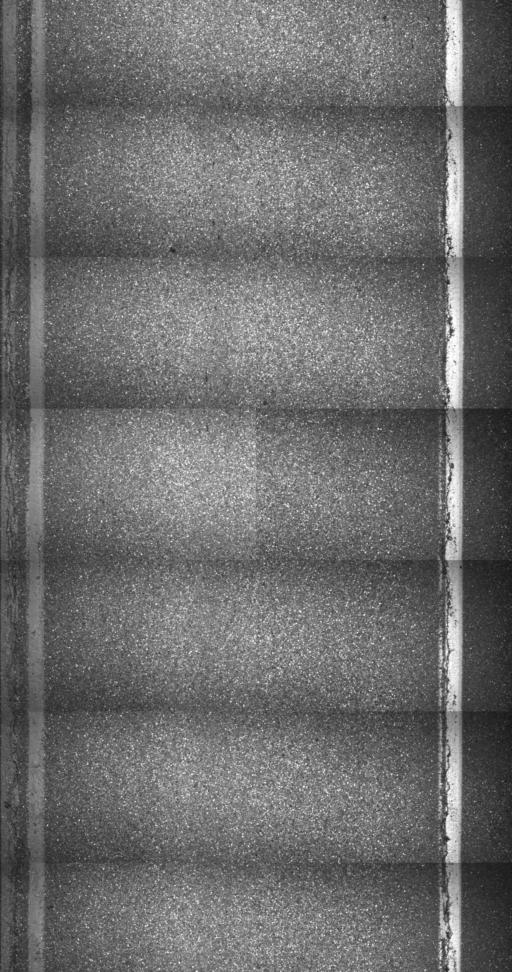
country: US
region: Vermont
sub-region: Rutland County
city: Fair Haven
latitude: 43.6615
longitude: -73.2910
